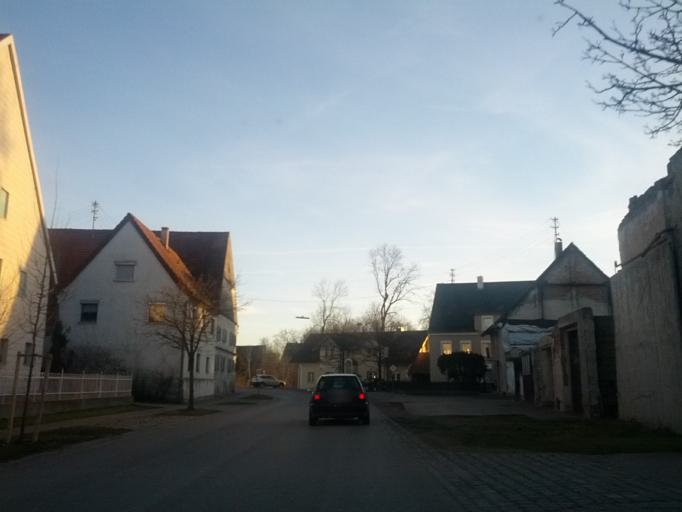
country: DE
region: Bavaria
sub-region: Swabia
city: Fellheim
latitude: 48.0930
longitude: 10.1508
